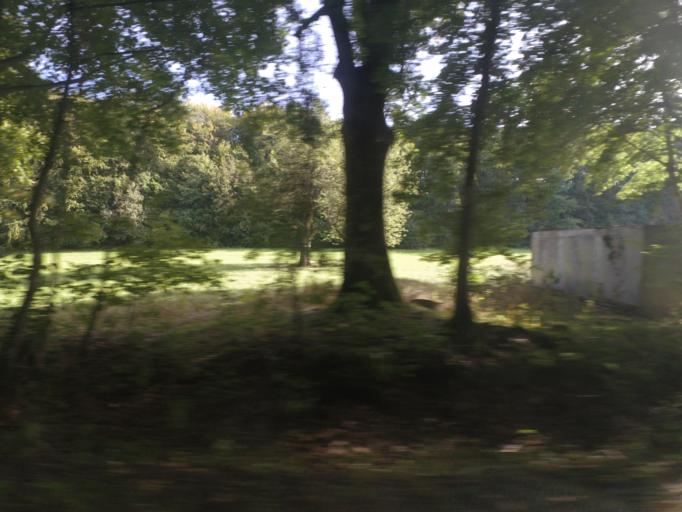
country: DE
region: Bavaria
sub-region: Regierungsbezirk Unterfranken
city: Hausen
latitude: 50.5061
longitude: 10.1143
